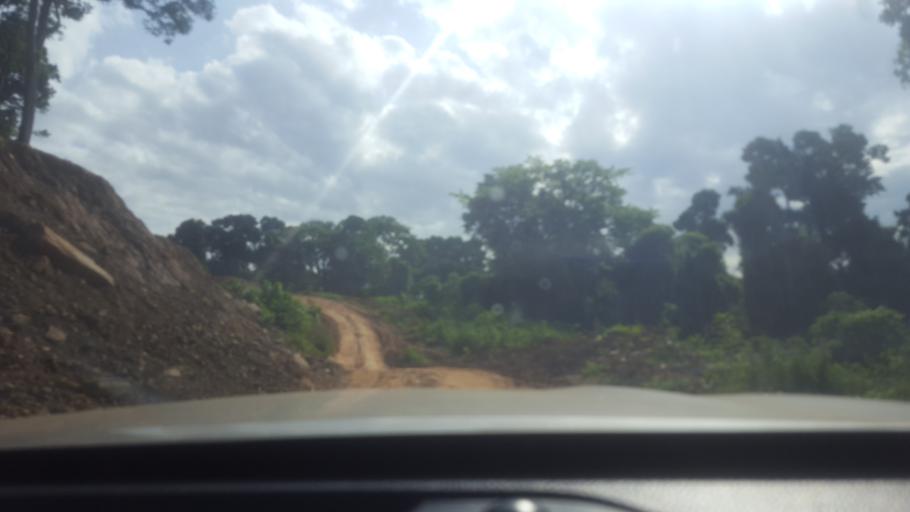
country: ET
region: Southern Nations, Nationalities, and People's Region
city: Tippi
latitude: 7.5313
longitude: 34.9845
